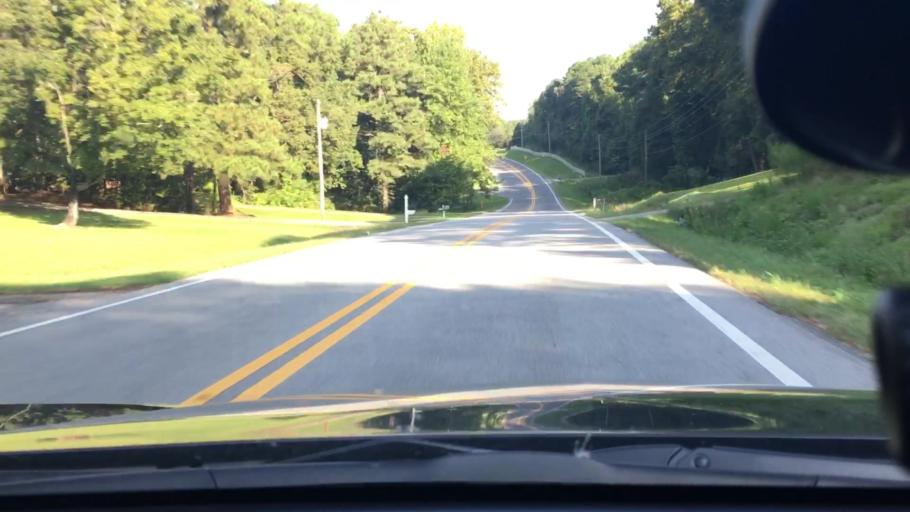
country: US
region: North Carolina
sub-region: Pitt County
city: Summerfield
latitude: 35.6414
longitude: -77.4544
